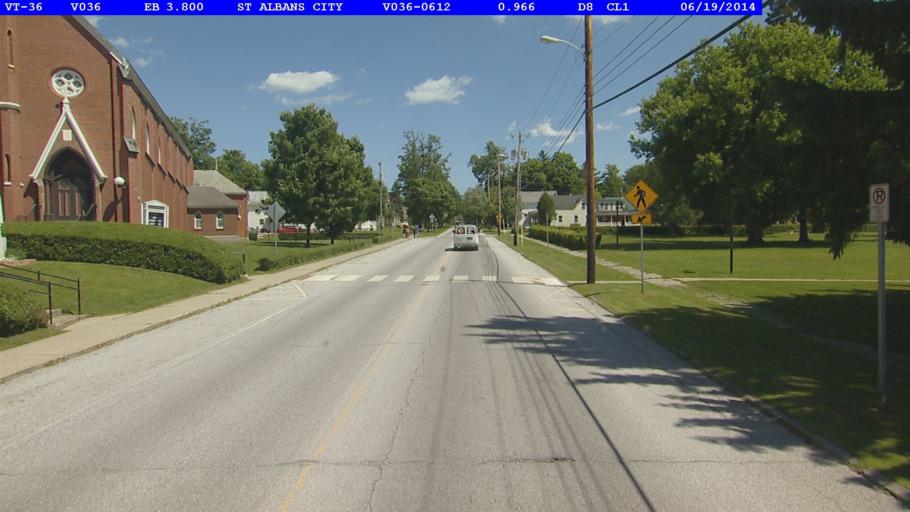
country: US
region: Vermont
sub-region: Franklin County
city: Saint Albans
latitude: 44.8099
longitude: -73.0815
